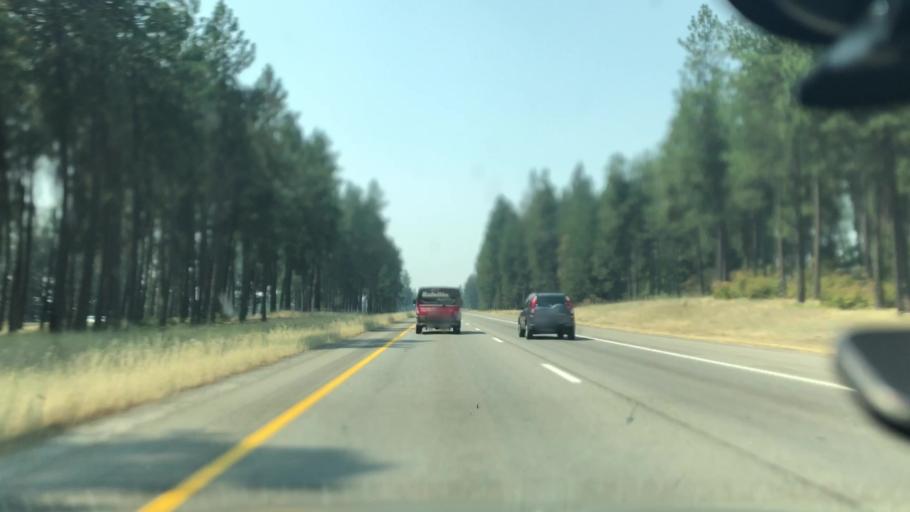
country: US
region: Idaho
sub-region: Kootenai County
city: Coeur d'Alene
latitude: 47.7064
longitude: -116.8434
